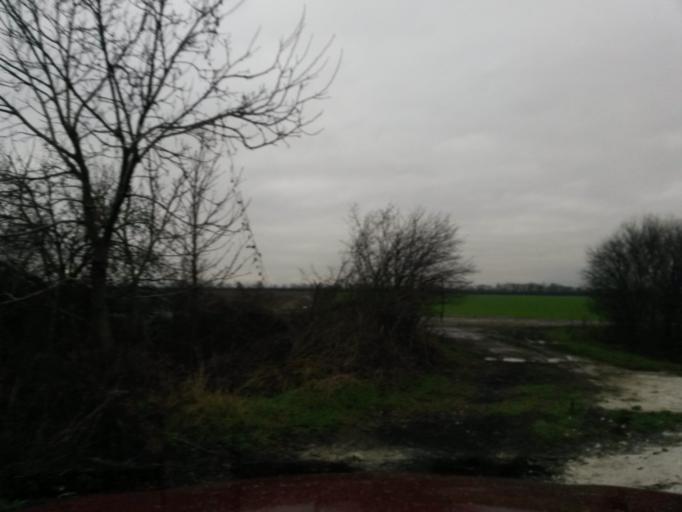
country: SK
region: Kosicky
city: Sobrance
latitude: 48.6507
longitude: 22.0696
